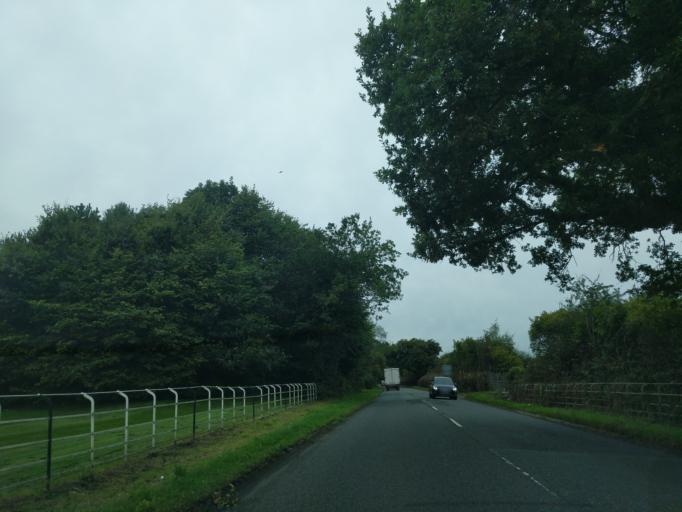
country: GB
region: England
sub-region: Cheshire East
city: Weston
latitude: 53.0568
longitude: -2.3939
